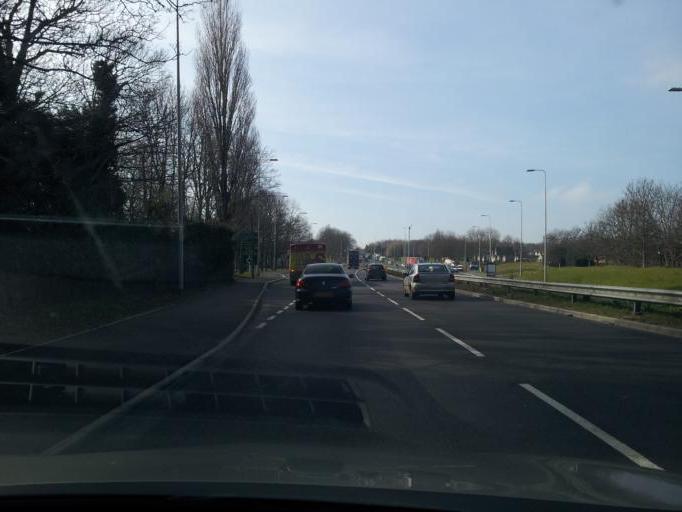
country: GB
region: England
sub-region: Nottinghamshire
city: Ruddington
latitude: 52.9169
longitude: -1.1747
